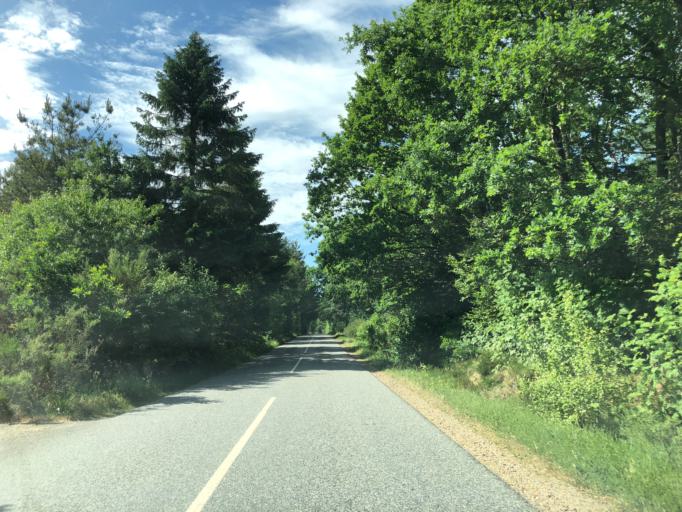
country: DK
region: Central Jutland
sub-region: Herning Kommune
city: Lind
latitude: 56.0319
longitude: 8.9470
